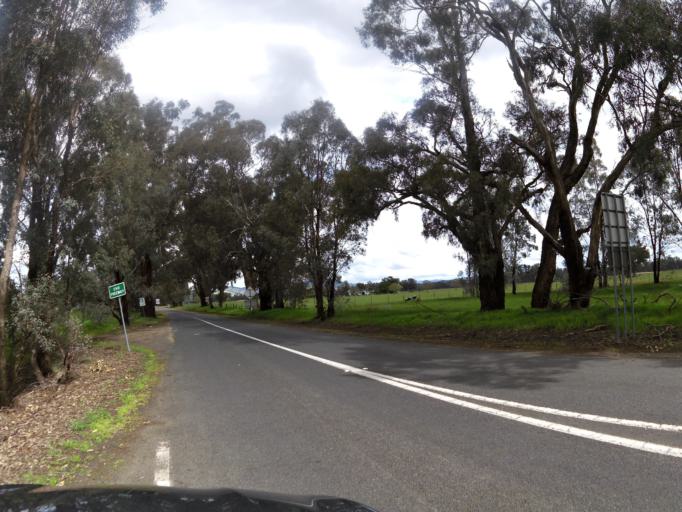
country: AU
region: Victoria
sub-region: Benalla
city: Benalla
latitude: -36.6019
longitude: 145.8671
